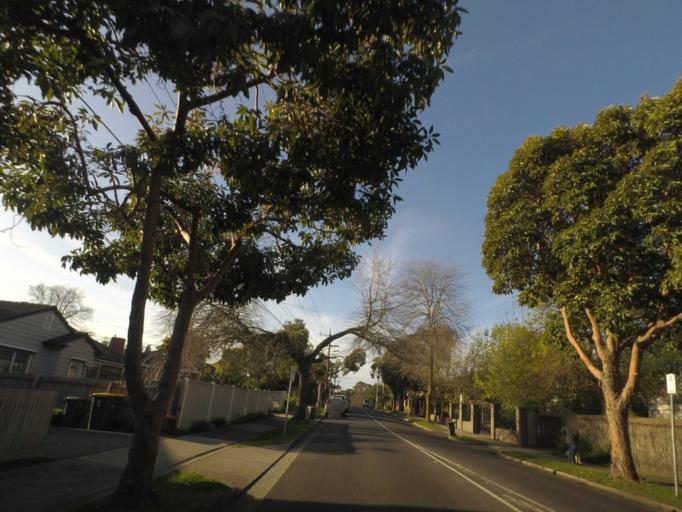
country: AU
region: Victoria
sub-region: Whitehorse
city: Blackburn
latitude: -37.8156
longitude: 145.1503
